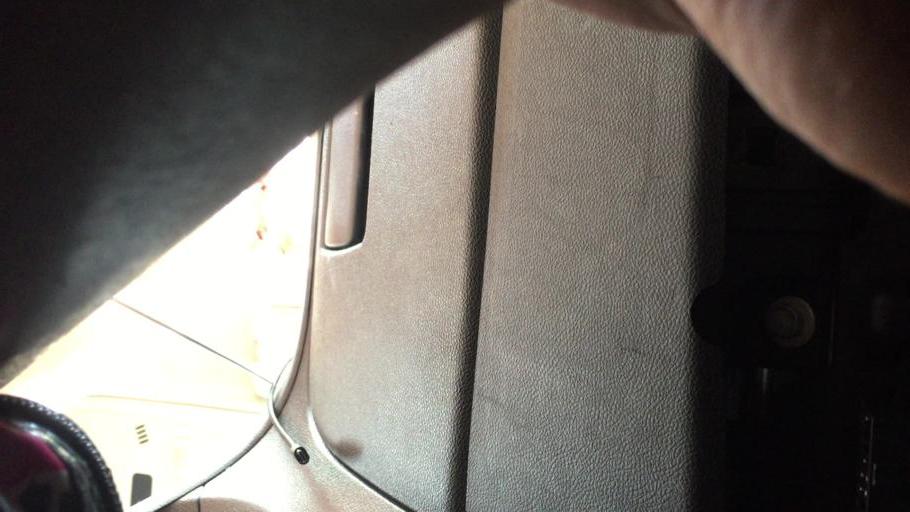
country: US
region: Georgia
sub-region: Carroll County
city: Carrollton
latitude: 33.6023
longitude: -85.0271
